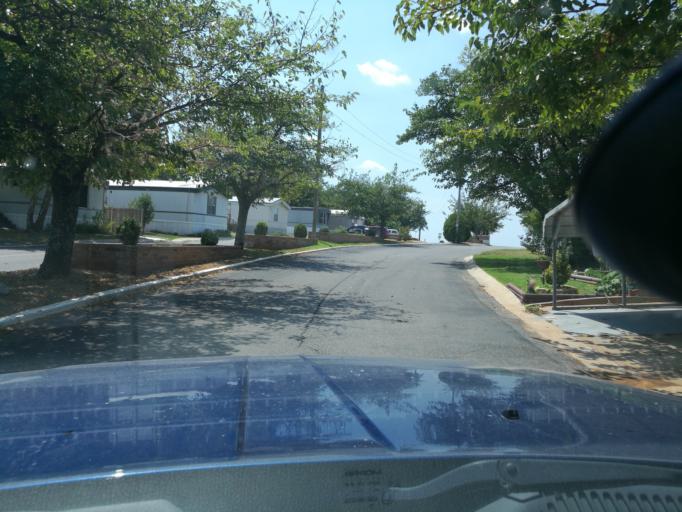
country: US
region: Oklahoma
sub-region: Oklahoma County
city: Del City
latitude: 35.4171
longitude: -97.4726
